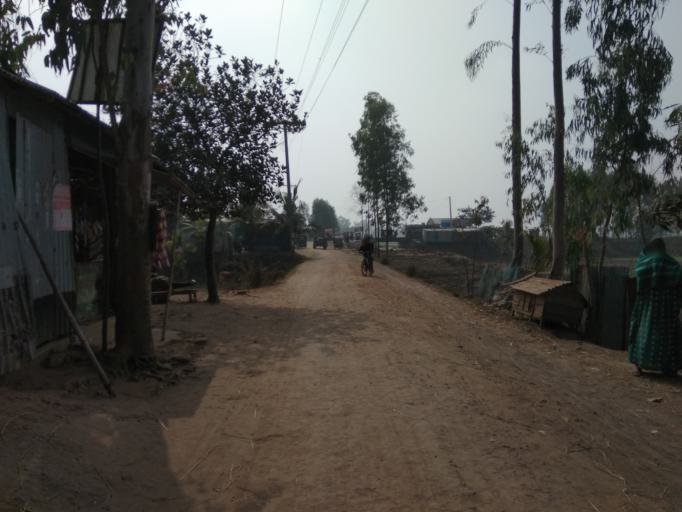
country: BD
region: Rajshahi
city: Bogra
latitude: 24.4775
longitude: 89.2668
